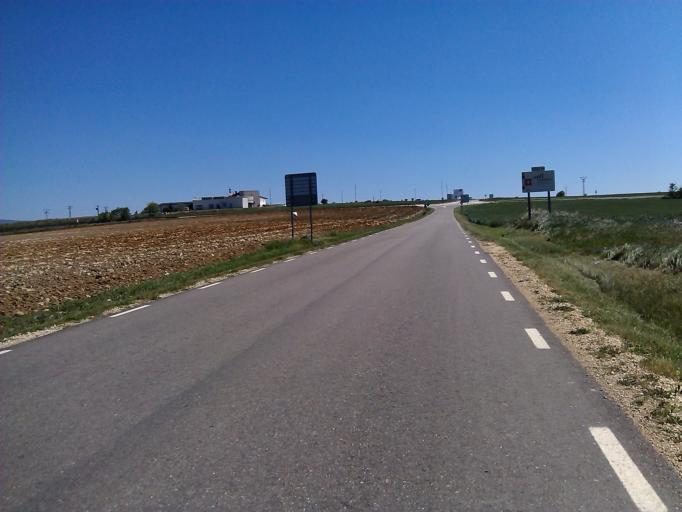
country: ES
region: Castille and Leon
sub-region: Provincia de Burgos
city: Arlanzon
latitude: 42.3529
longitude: -3.4632
